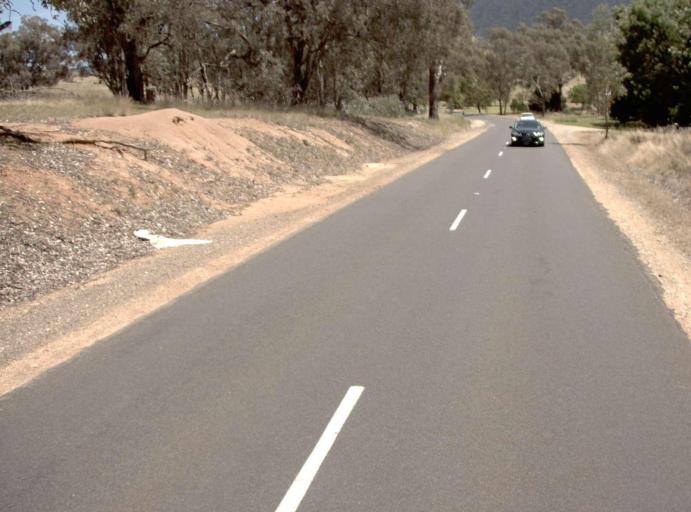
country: AU
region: Victoria
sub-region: East Gippsland
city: Bairnsdale
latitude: -37.1804
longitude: 147.7075
